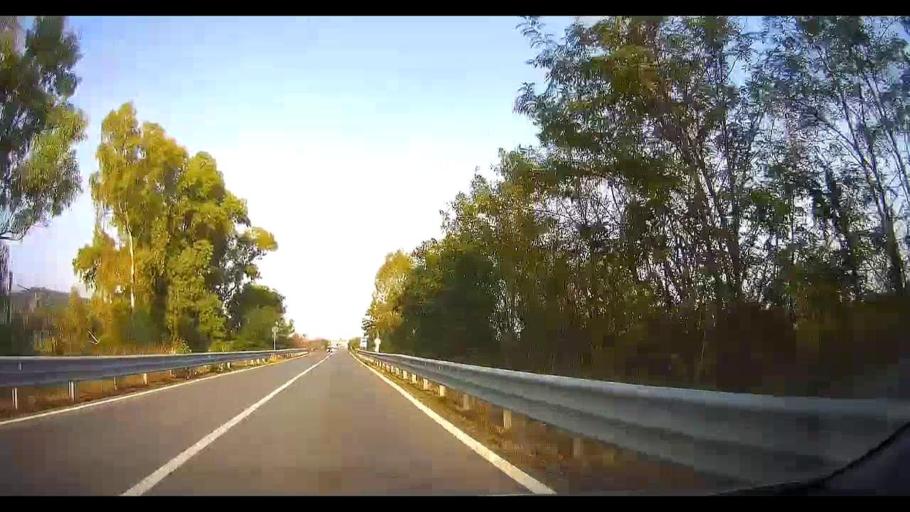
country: IT
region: Calabria
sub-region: Provincia di Cosenza
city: Cariati
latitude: 39.5216
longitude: 16.9009
